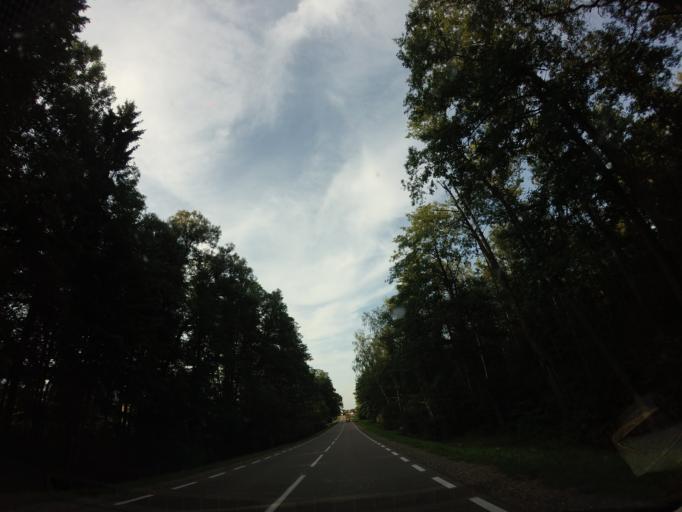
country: PL
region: Podlasie
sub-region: Powiat sejnenski
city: Sejny
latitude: 54.0343
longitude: 23.3543
